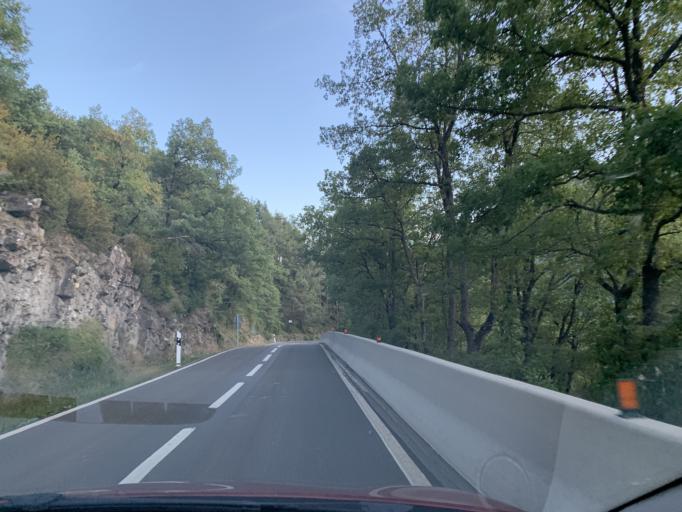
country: ES
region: Aragon
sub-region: Provincia de Huesca
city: Broto
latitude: 42.5946
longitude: -0.1180
